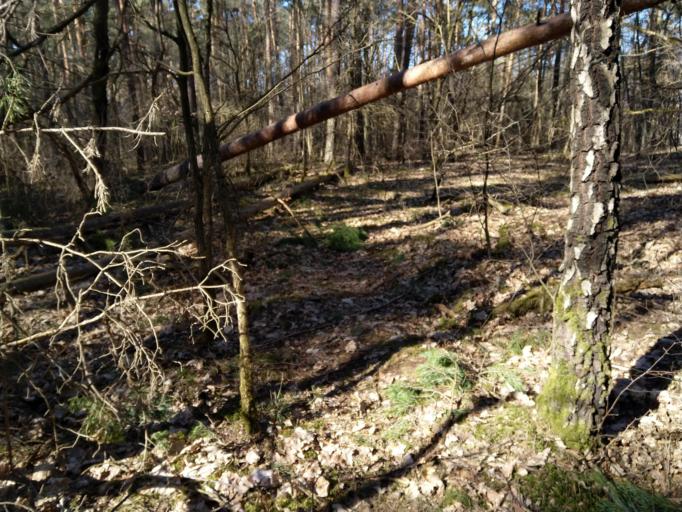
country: DE
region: Brandenburg
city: Grunheide
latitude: 52.4142
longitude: 13.8142
